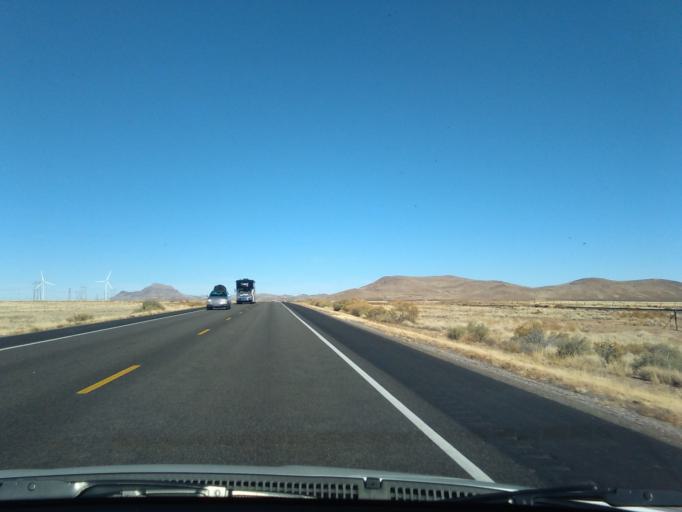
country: US
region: New Mexico
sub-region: Luna County
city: Deming
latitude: 32.5118
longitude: -107.5039
